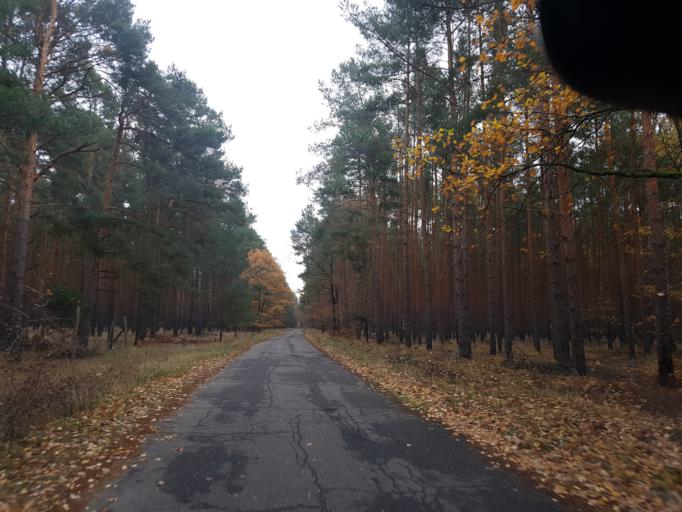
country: DE
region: Brandenburg
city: Treuenbrietzen
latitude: 52.1063
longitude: 12.9137
